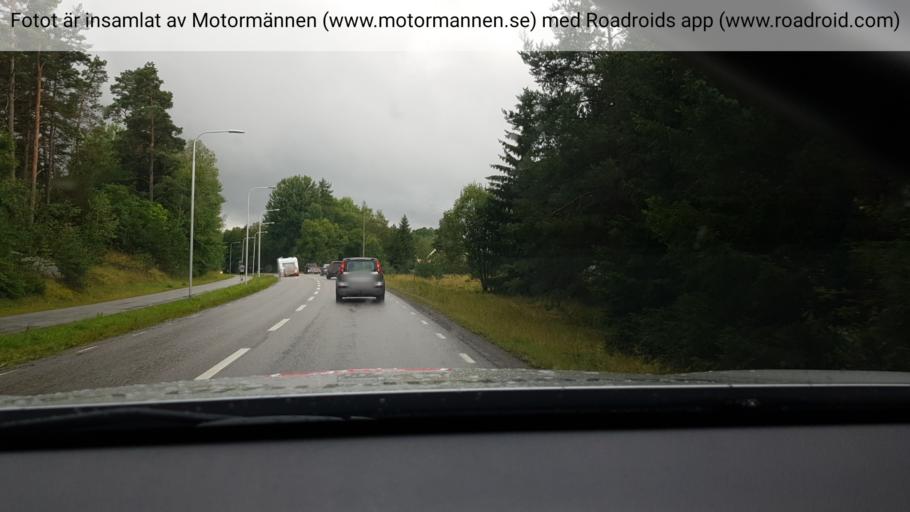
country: SE
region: Stockholm
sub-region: Haninge Kommun
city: Jordbro
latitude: 59.1173
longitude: 18.0641
